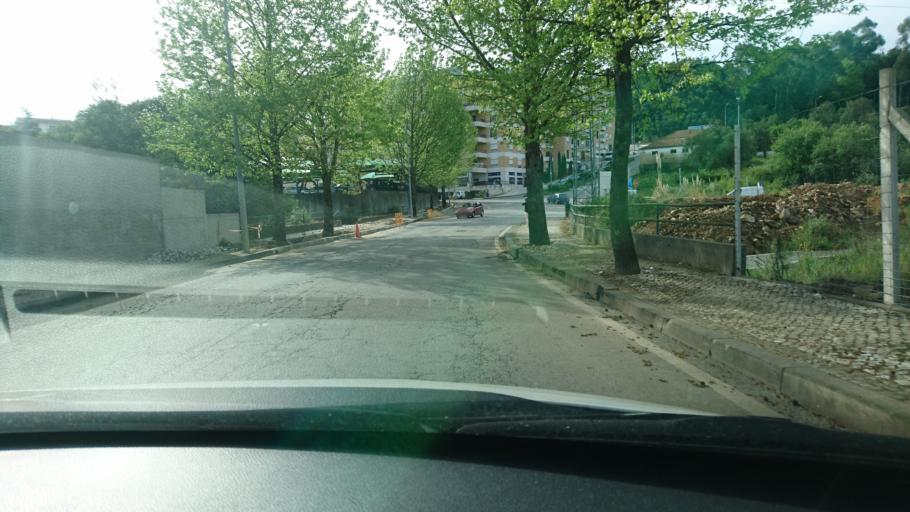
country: PT
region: Aveiro
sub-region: Oliveira de Azemeis
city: Oliveira de Azemeis
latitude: 40.8461
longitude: -8.4785
